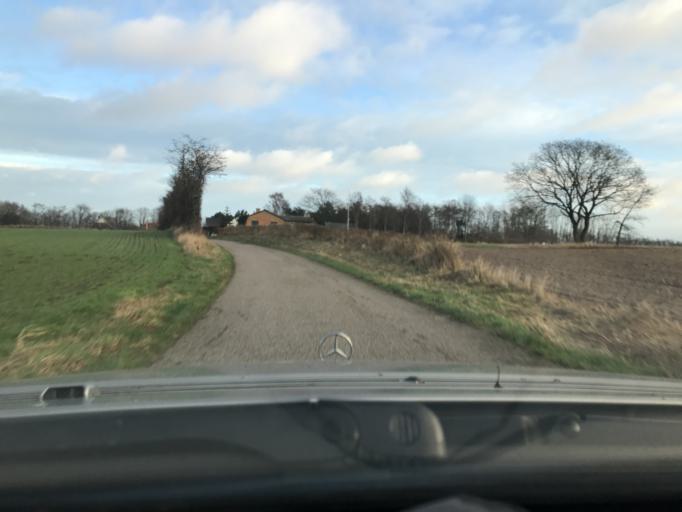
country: DK
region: South Denmark
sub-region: Sonderborg Kommune
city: Nordborg
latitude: 55.0496
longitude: 9.6776
